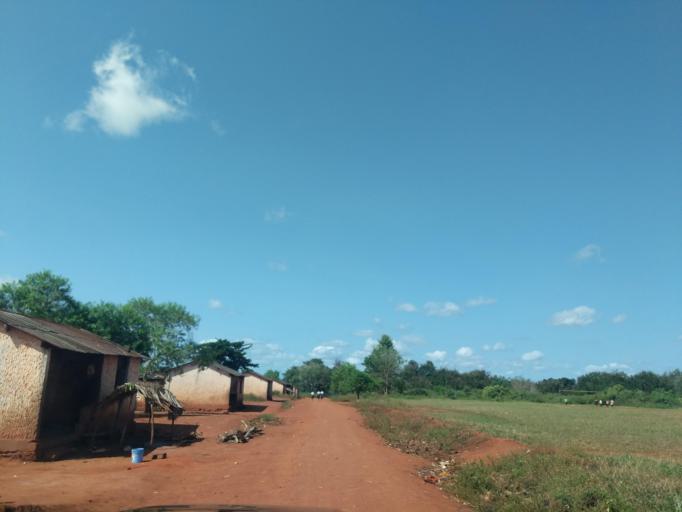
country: TZ
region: Tanga
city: Muheza
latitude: -5.3882
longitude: 38.5753
